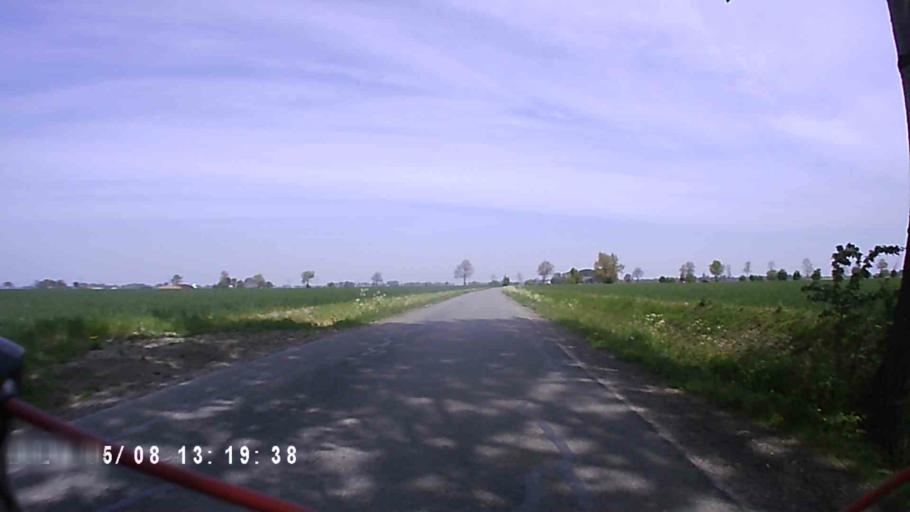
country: NL
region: Groningen
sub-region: Gemeente Bedum
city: Bedum
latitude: 53.3165
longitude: 6.7162
